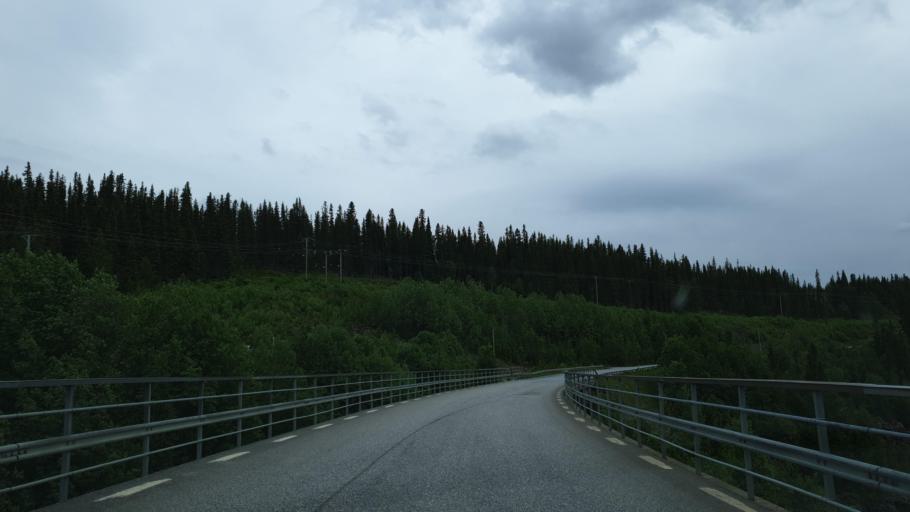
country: SE
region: Vaesterbotten
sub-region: Storumans Kommun
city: Fristad
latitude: 65.4240
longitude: 16.1717
